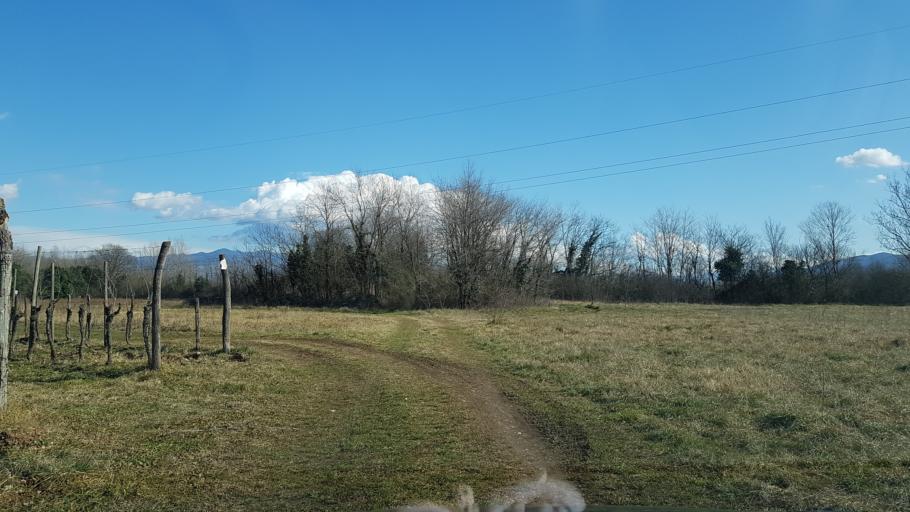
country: IT
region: Friuli Venezia Giulia
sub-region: Provincia di Gorizia
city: Savogna d'Isonzo
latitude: 45.9096
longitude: 13.5564
